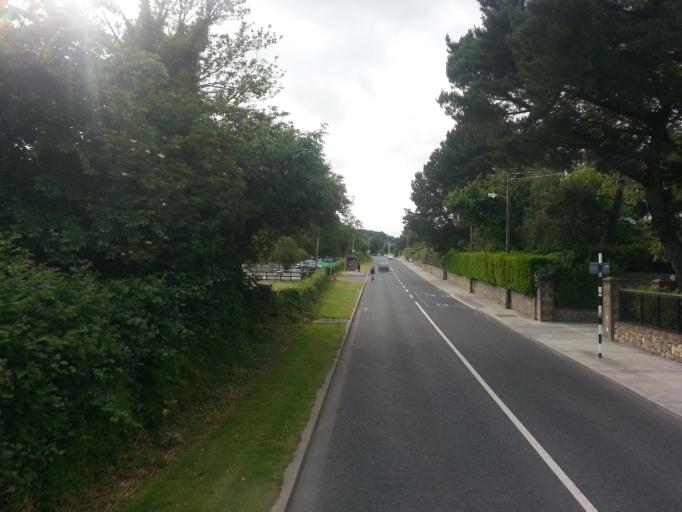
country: IE
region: Leinster
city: Sandyford
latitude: 53.2492
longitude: -6.2064
